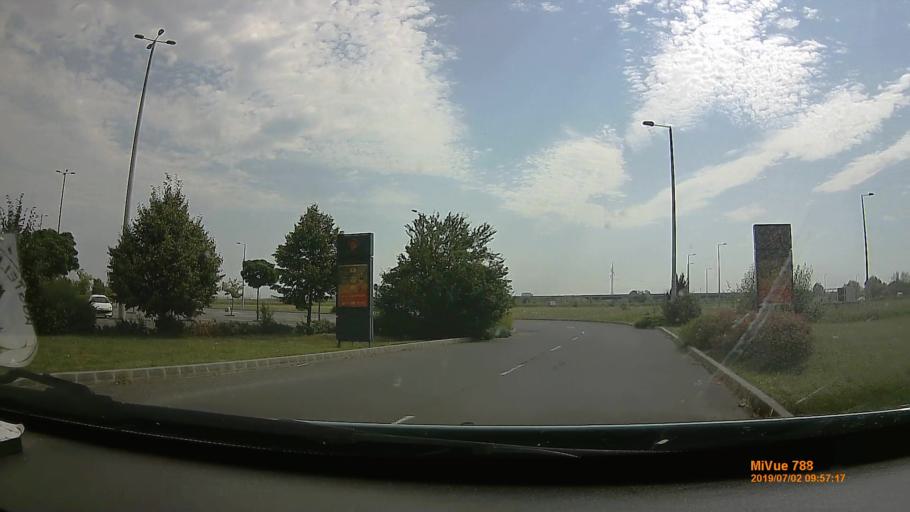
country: HU
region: Borsod-Abauj-Zemplen
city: Felsozsolca
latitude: 48.1076
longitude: 20.8375
